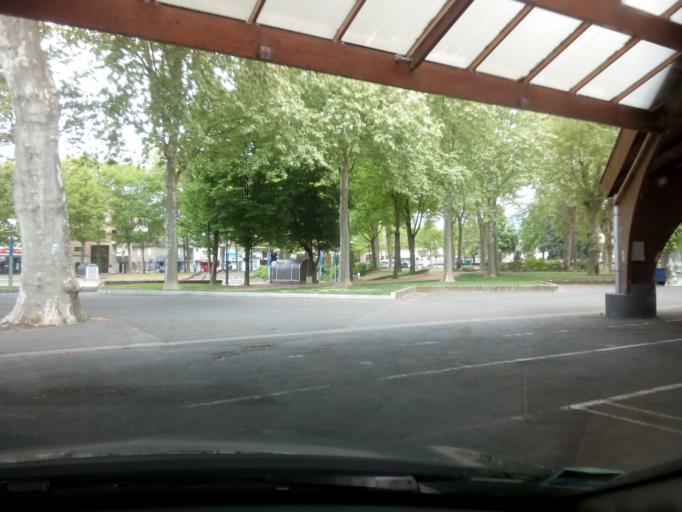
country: FR
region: Limousin
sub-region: Departement de la Correze
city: Brive-la-Gaillarde
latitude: 45.1629
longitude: 1.5344
